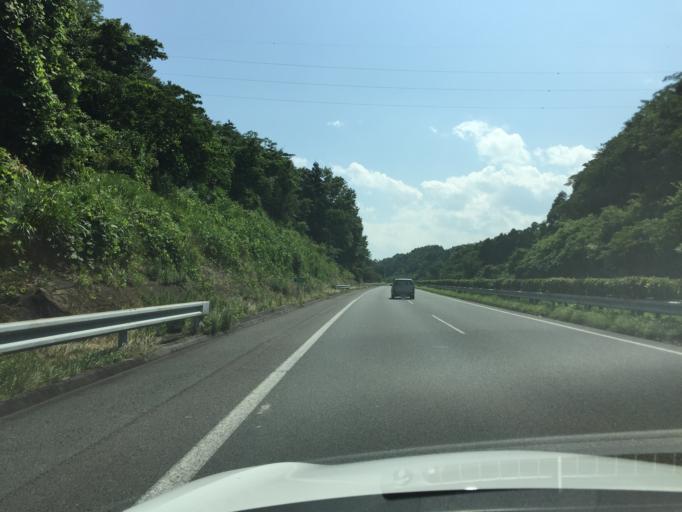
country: JP
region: Fukushima
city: Iwaki
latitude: 36.9697
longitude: 140.7906
